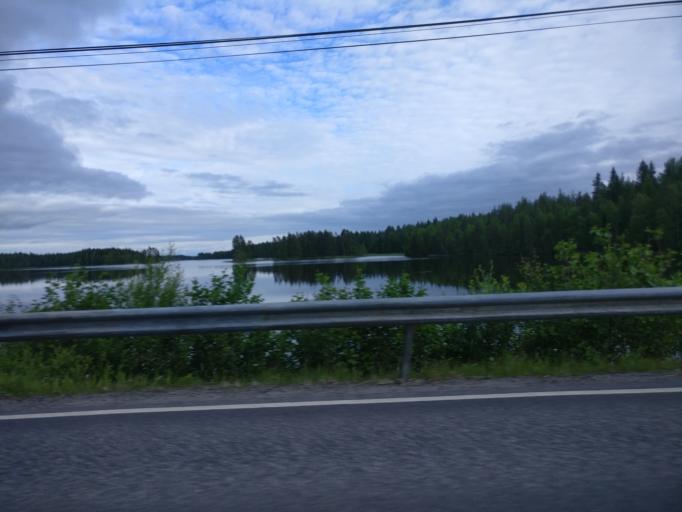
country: FI
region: Southern Savonia
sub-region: Savonlinna
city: Savonlinna
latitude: 61.9571
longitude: 28.9267
